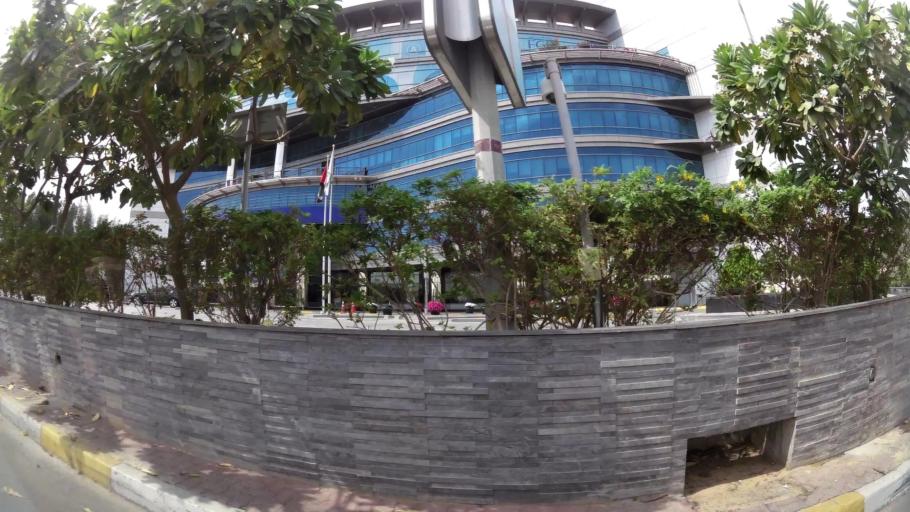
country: AE
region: Abu Dhabi
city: Abu Dhabi
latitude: 24.4638
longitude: 54.3361
